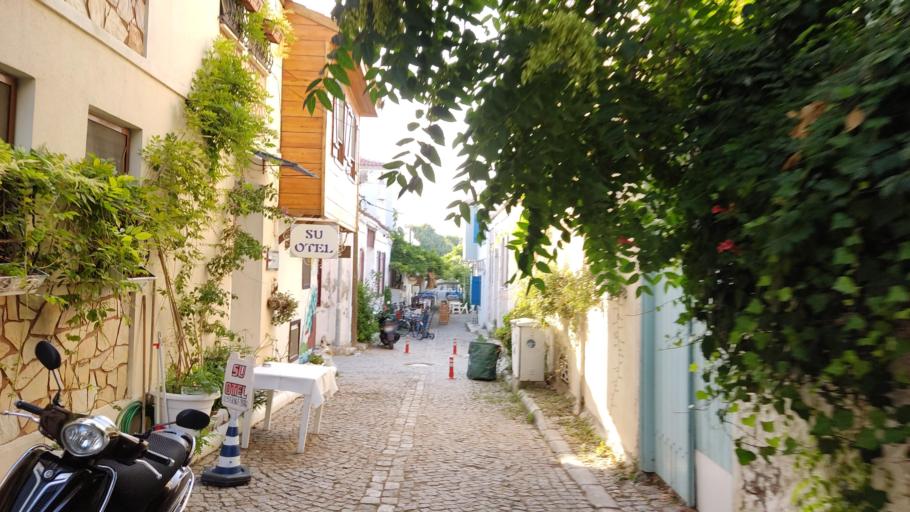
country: TR
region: Canakkale
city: Bozcaada
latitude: 39.8357
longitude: 26.0692
